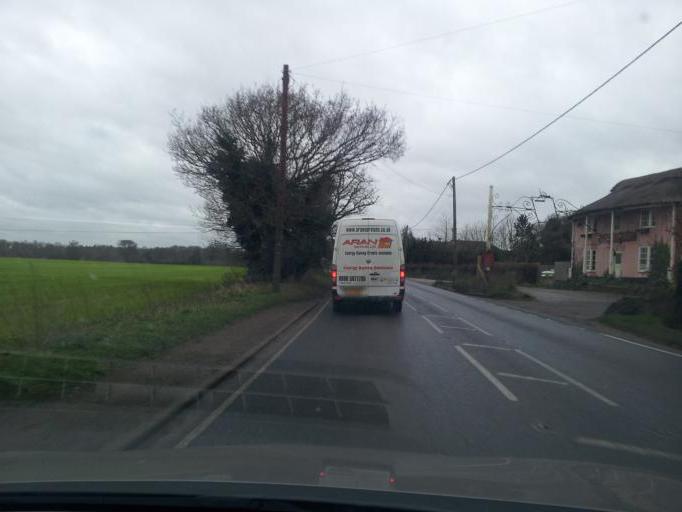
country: GB
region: England
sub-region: Suffolk
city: Ixworth
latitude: 52.3222
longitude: 0.8738
